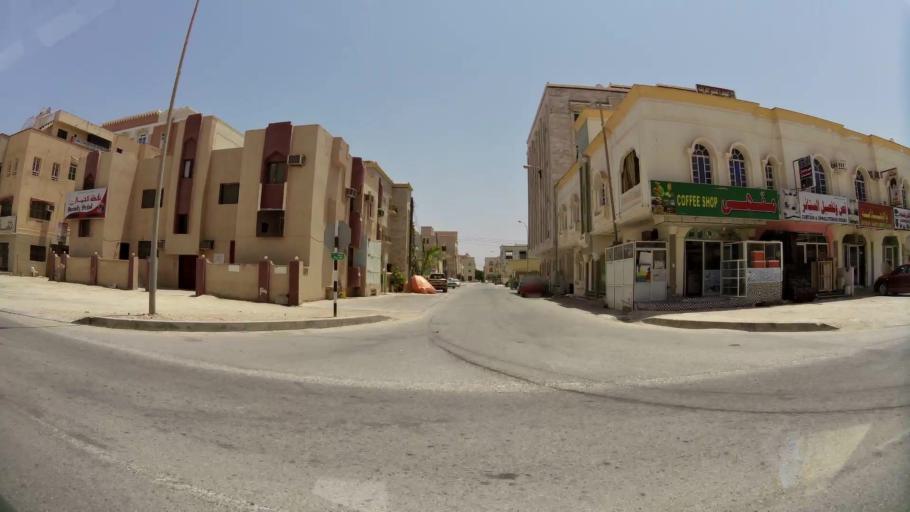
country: OM
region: Zufar
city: Salalah
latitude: 17.0204
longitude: 54.0802
